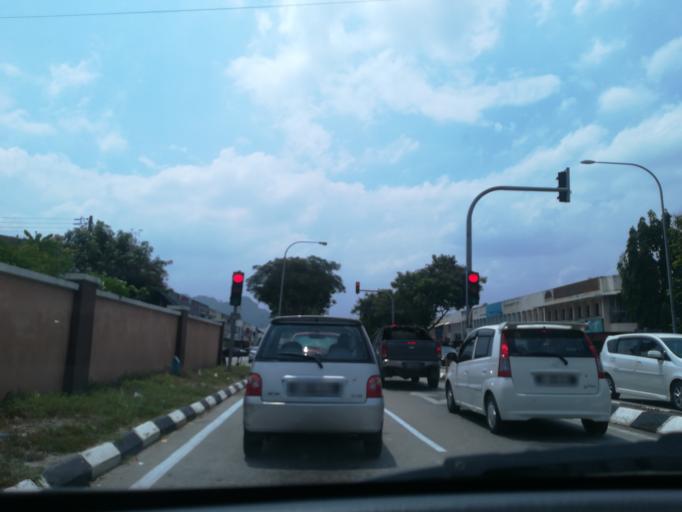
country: MY
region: Perak
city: Ipoh
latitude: 4.5723
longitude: 101.1261
